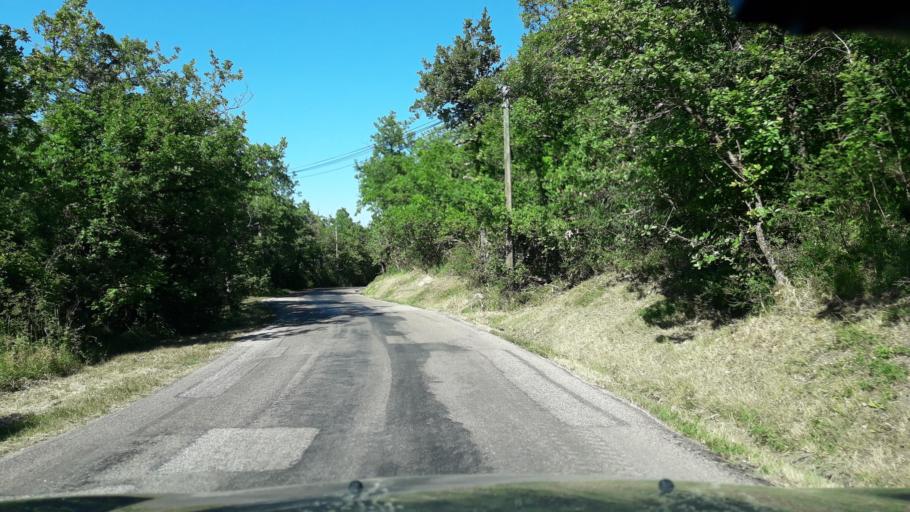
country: FR
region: Rhone-Alpes
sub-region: Departement de l'Ardeche
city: Privas
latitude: 44.7076
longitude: 4.5910
